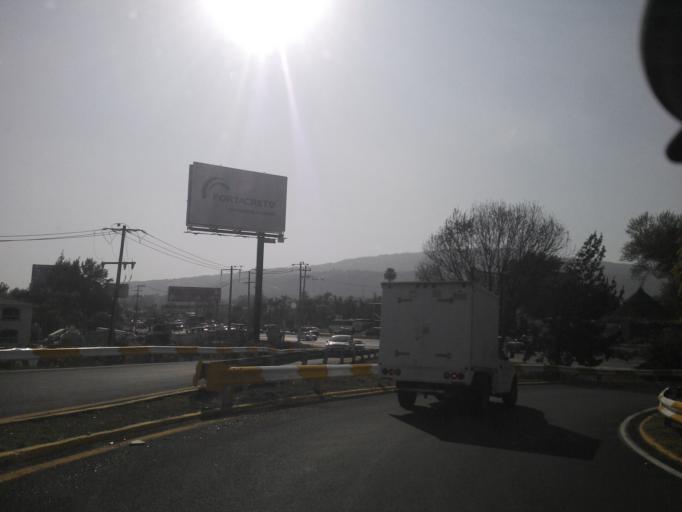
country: MX
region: Jalisco
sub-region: Tlajomulco de Zuniga
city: La Tijera
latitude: 20.6024
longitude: -103.4343
